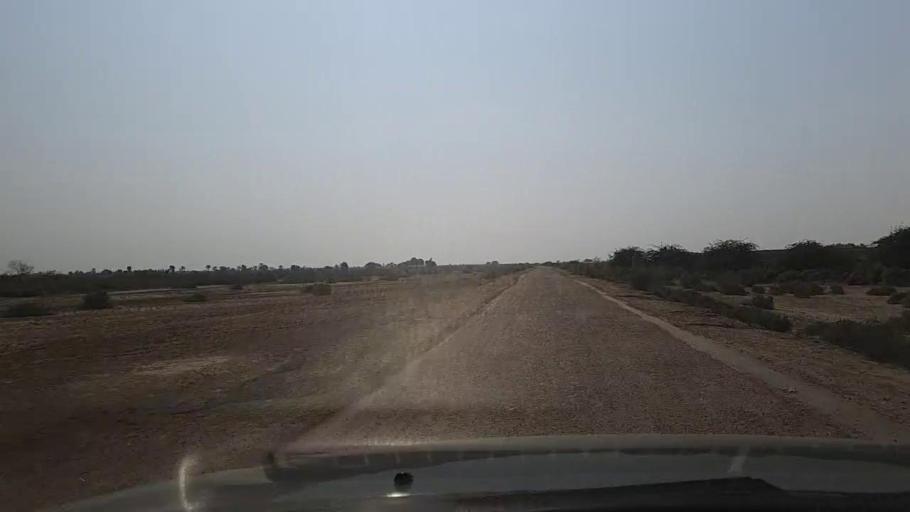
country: PK
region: Sindh
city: Mirpur Sakro
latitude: 24.3864
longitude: 67.6637
